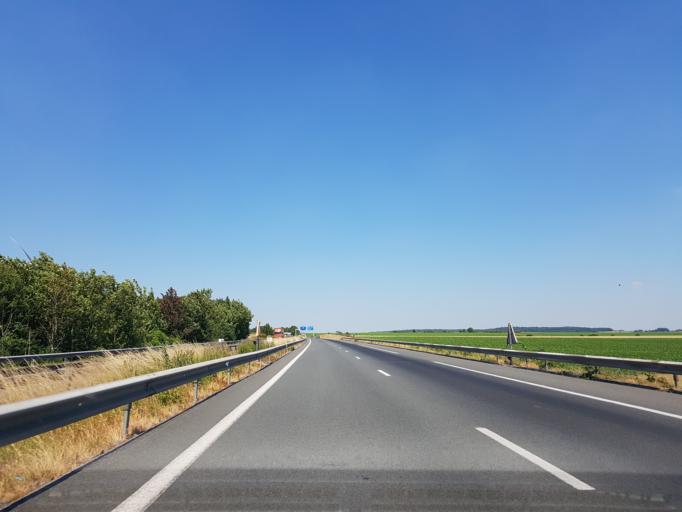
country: FR
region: Nord-Pas-de-Calais
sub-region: Departement du Nord
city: Marcoing
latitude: 50.1296
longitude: 3.1485
